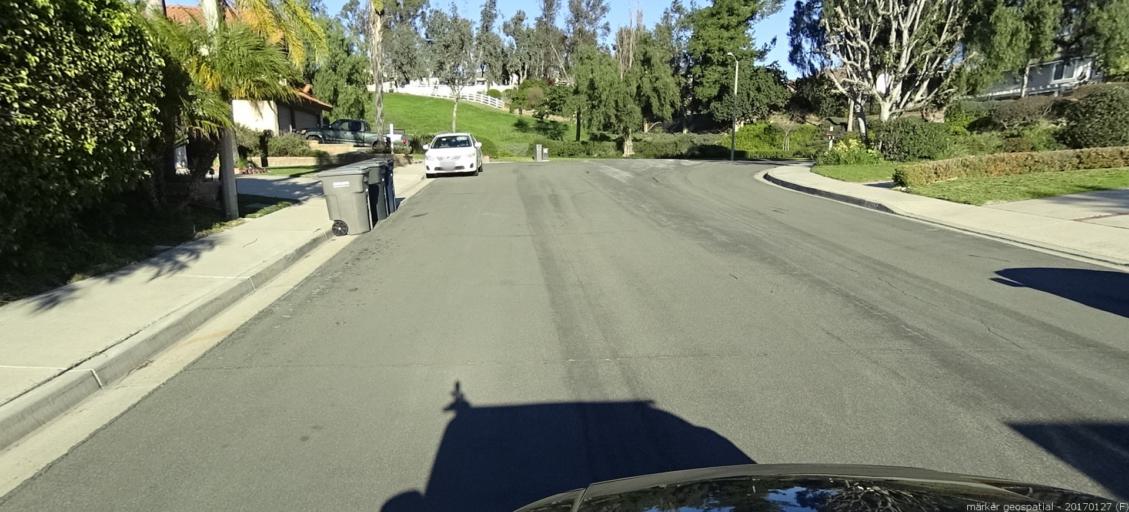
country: US
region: California
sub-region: Orange County
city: Lake Forest
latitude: 33.6461
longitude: -117.6695
